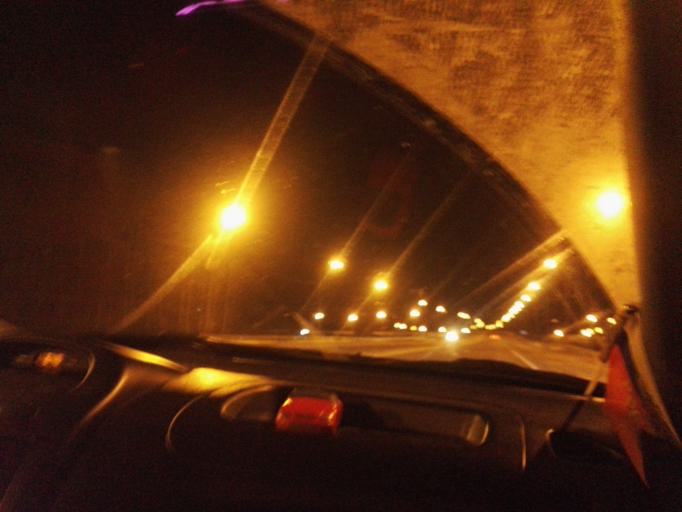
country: RU
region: Tula
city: Gritsovskiy
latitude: 54.0708
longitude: 38.1554
